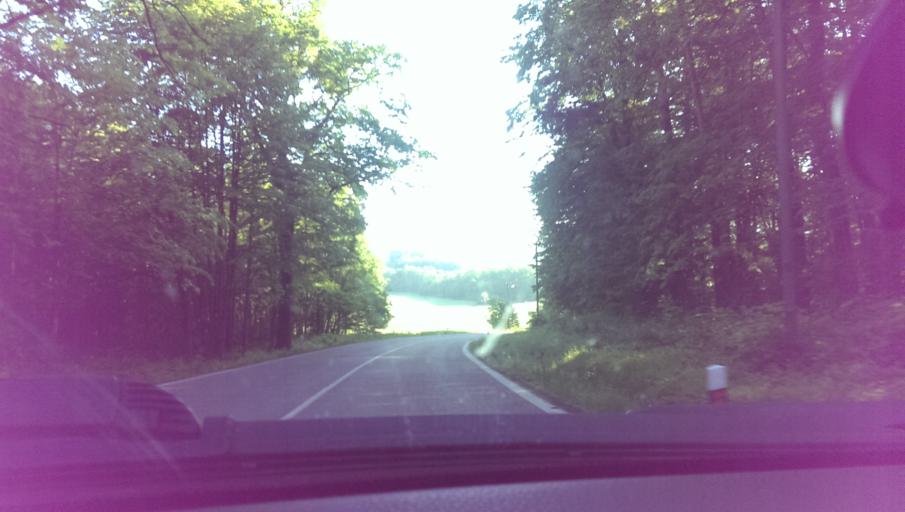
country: CZ
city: Kuncice pod Ondrejnikem
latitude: 49.5478
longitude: 18.2423
